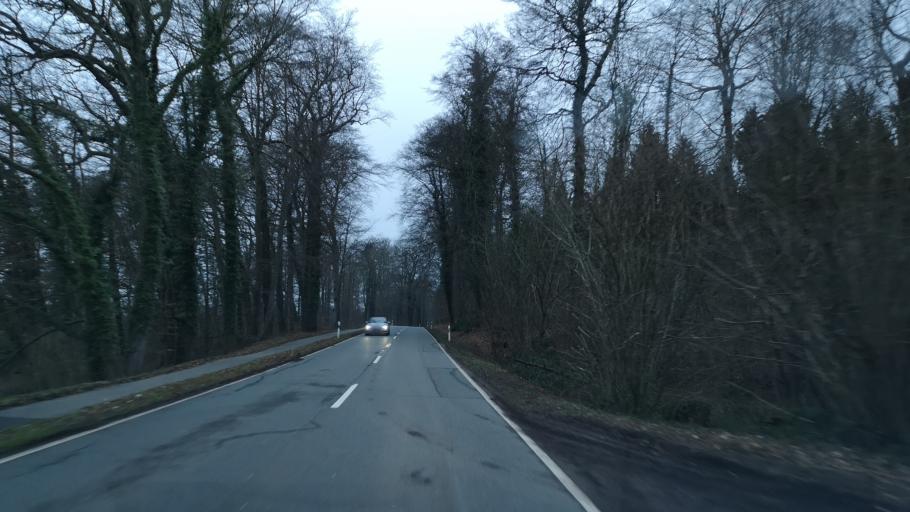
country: DE
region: Schleswig-Holstein
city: Munsterdorf
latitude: 53.9147
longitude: 9.5377
